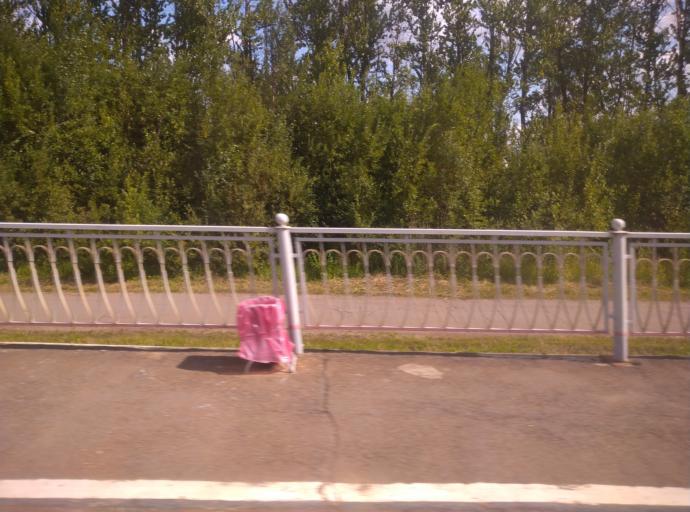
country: RU
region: St.-Petersburg
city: Obukhovo
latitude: 59.8797
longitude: 30.4069
